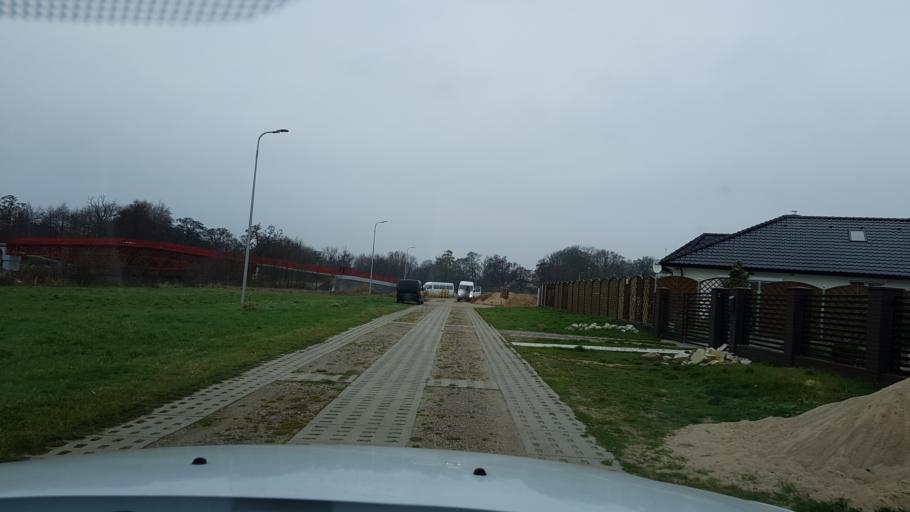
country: PL
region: West Pomeranian Voivodeship
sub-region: Powiat slawienski
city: Darlowo
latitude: 54.4154
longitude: 16.4180
